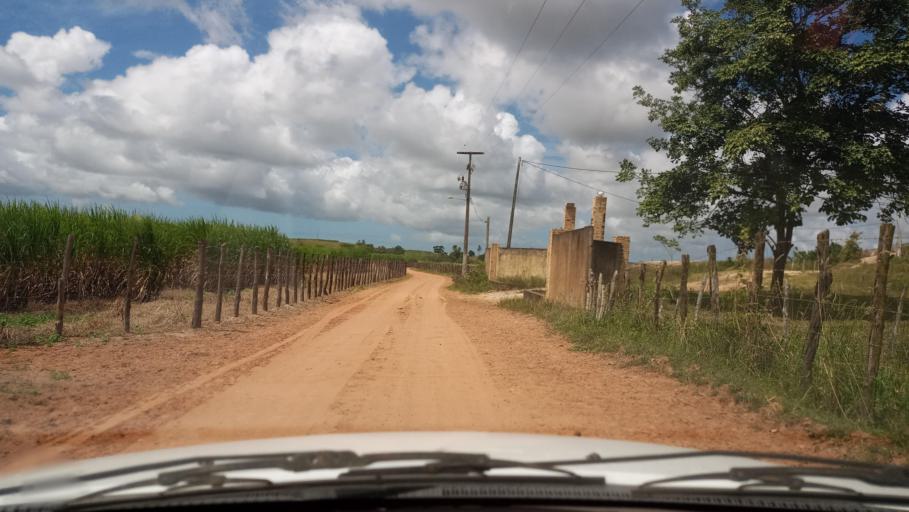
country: BR
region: Rio Grande do Norte
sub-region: Goianinha
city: Goianinha
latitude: -6.2605
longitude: -35.2449
